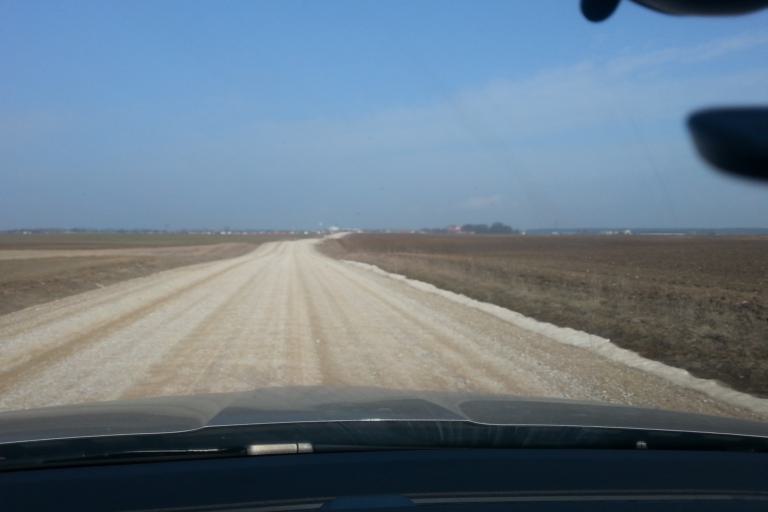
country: LT
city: Trakai
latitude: 54.5937
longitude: 24.9776
